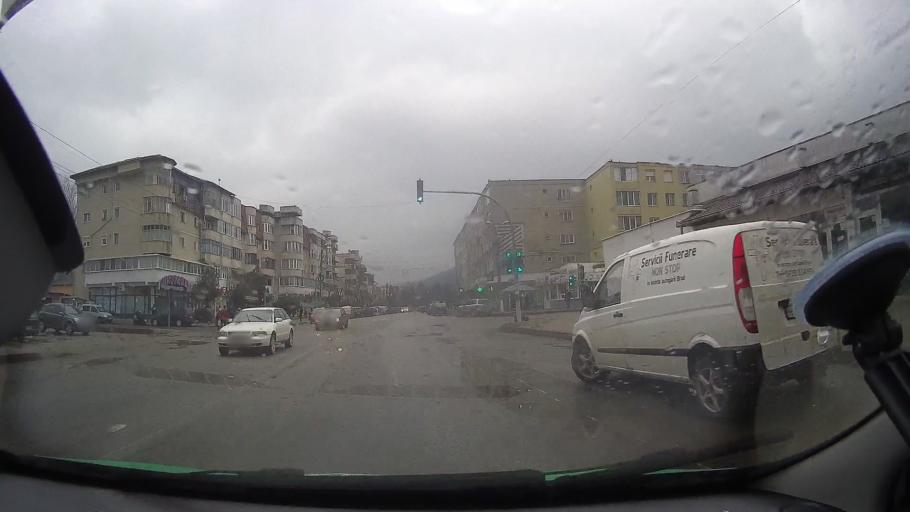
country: RO
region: Hunedoara
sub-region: Municipiul Brad
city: Brad
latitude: 46.1316
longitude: 22.7894
